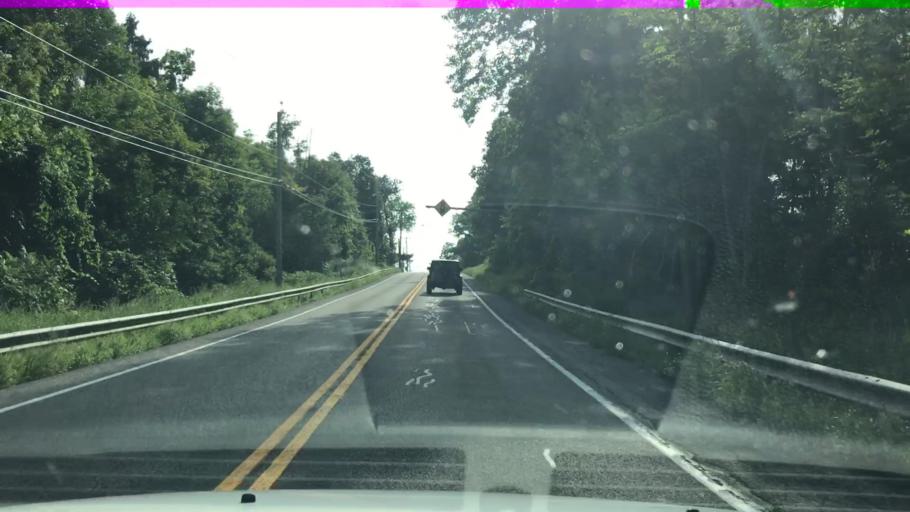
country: US
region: New York
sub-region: Erie County
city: Town Line
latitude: 42.8563
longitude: -78.5809
